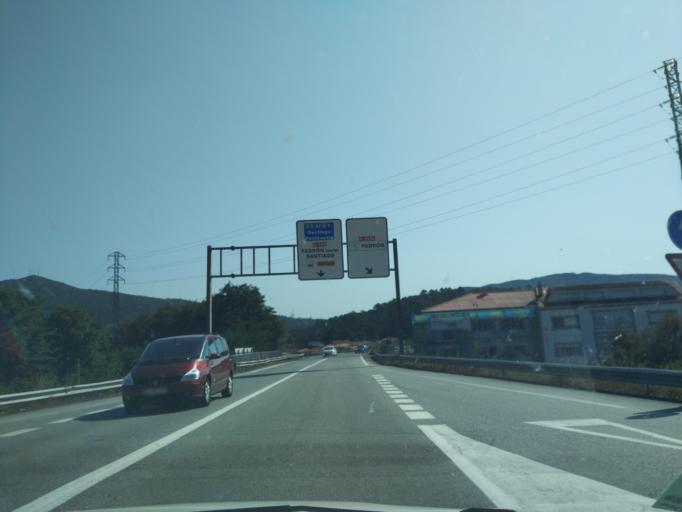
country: ES
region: Galicia
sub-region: Provincia da Coruna
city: Padron
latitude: 42.7315
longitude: -8.6590
